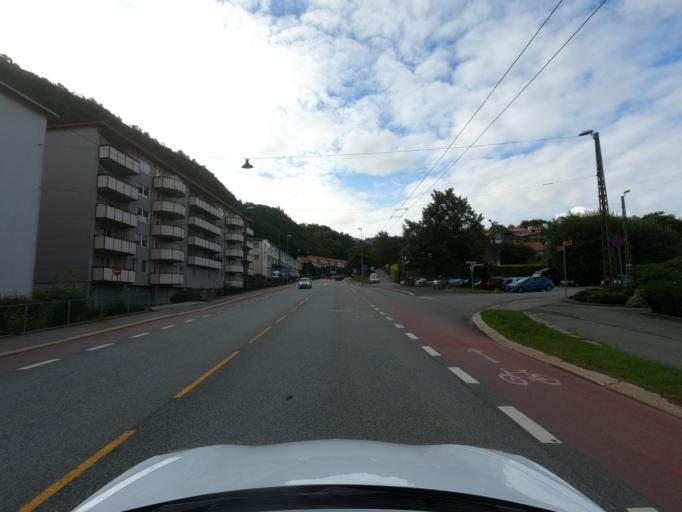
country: NO
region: Hordaland
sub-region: Bergen
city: Bergen
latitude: 60.3532
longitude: 5.3685
